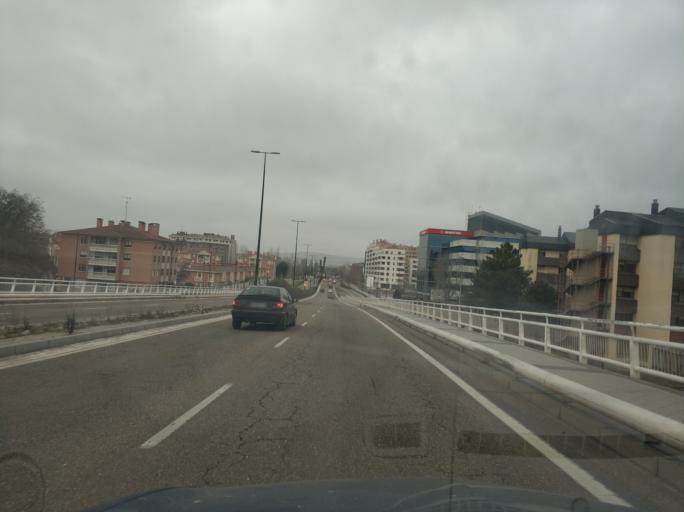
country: ES
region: Castille and Leon
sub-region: Provincia de Valladolid
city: Valladolid
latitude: 41.6216
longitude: -4.7424
